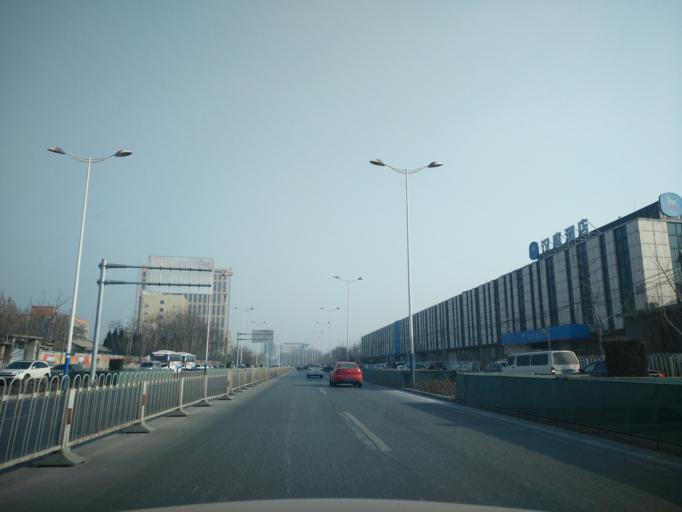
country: CN
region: Beijing
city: Daxing
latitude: 39.7421
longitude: 116.3181
